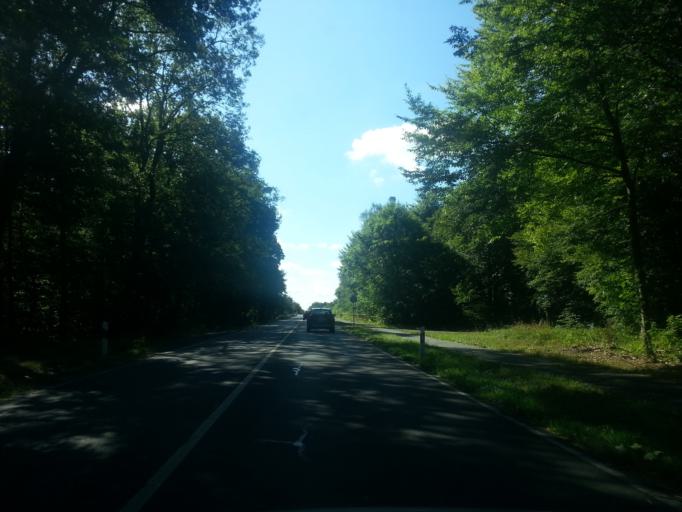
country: DE
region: Hesse
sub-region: Regierungsbezirk Darmstadt
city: Offenbach
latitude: 50.0693
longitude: 8.7662
